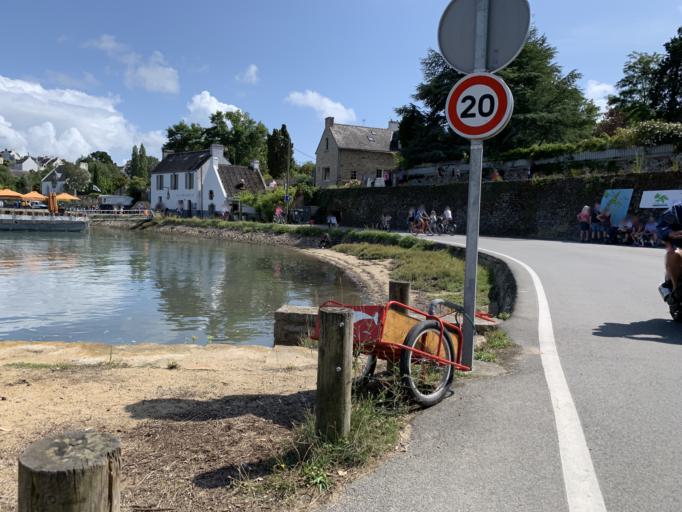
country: FR
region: Brittany
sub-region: Departement du Morbihan
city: Arradon
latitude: 47.5991
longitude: -2.8503
